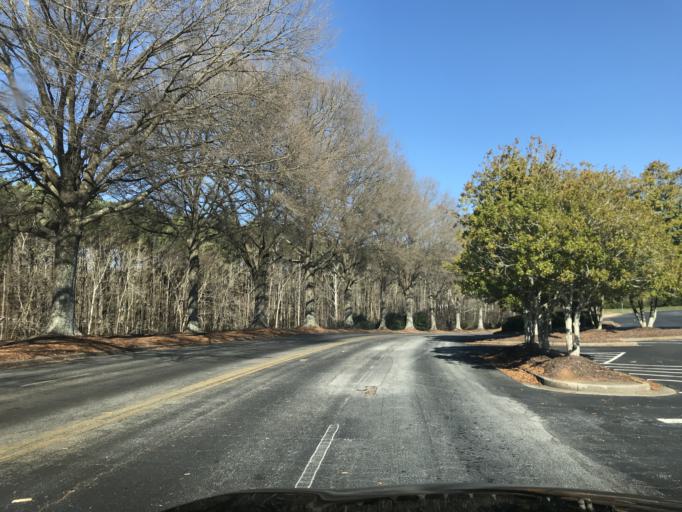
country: US
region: Georgia
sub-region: Clayton County
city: Morrow
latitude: 33.5746
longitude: -84.3555
